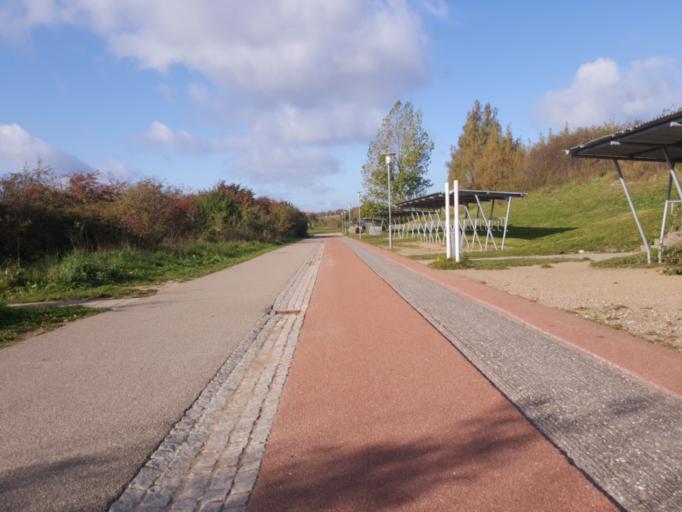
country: DK
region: Zealand
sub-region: Kalundborg Kommune
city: Kalundborg
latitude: 55.6915
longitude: 11.0829
